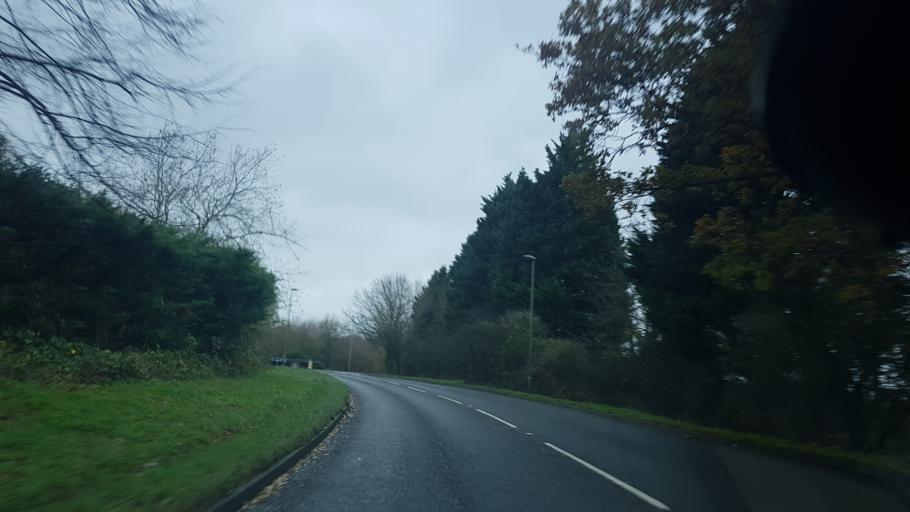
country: GB
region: England
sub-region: Surrey
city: Chilworth
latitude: 51.2512
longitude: -0.5261
